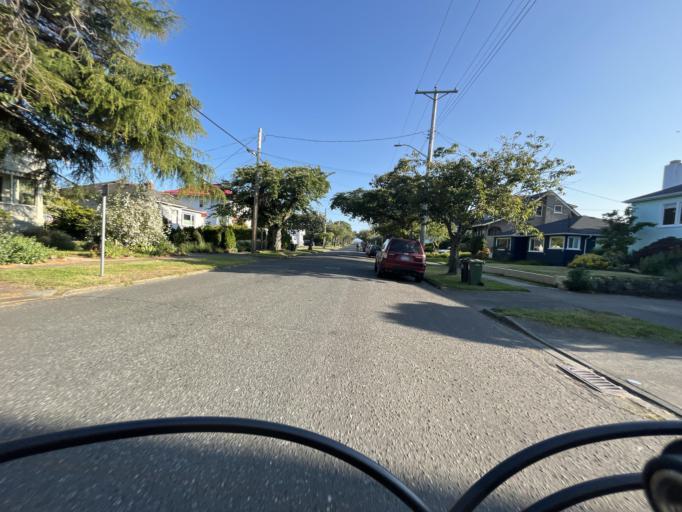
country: CA
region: British Columbia
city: Victoria
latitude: 48.4091
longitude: -123.3504
